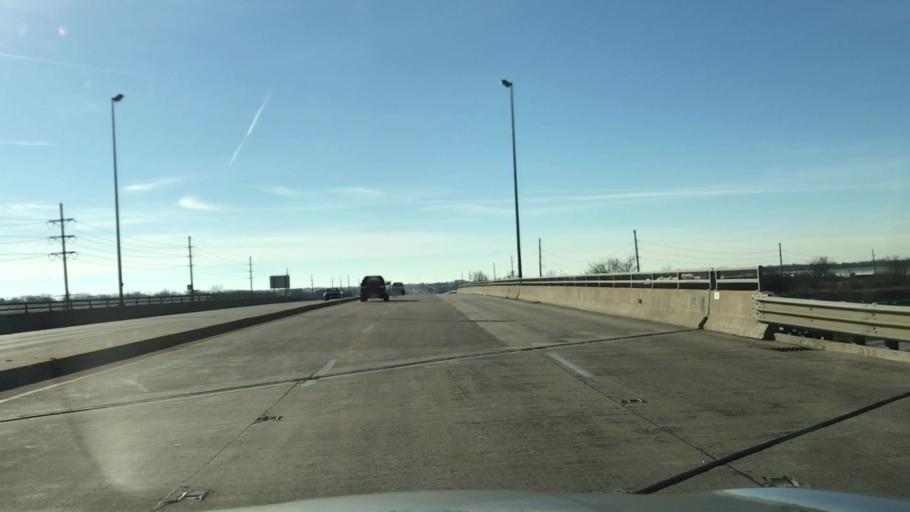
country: US
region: Illinois
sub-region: McLean County
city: Normal
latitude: 40.5300
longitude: -88.9518
